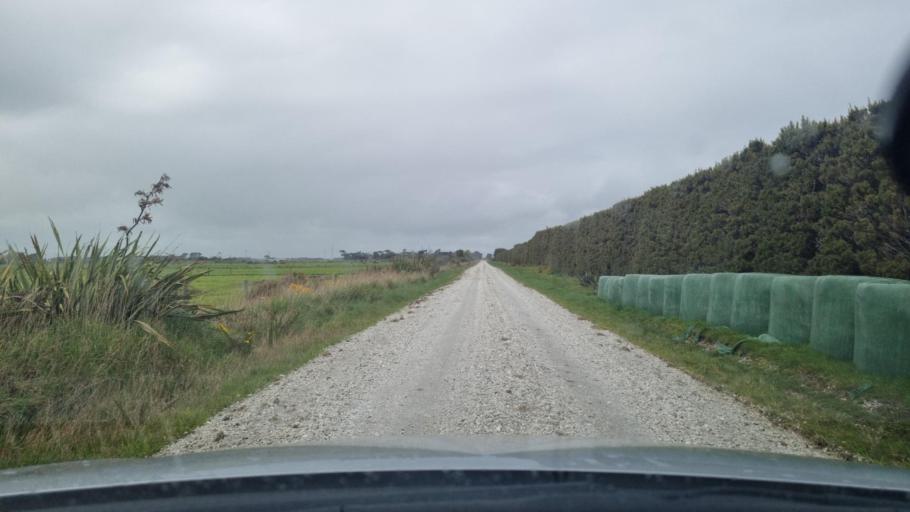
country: NZ
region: Southland
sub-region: Invercargill City
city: Invercargill
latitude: -46.4992
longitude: 168.4125
